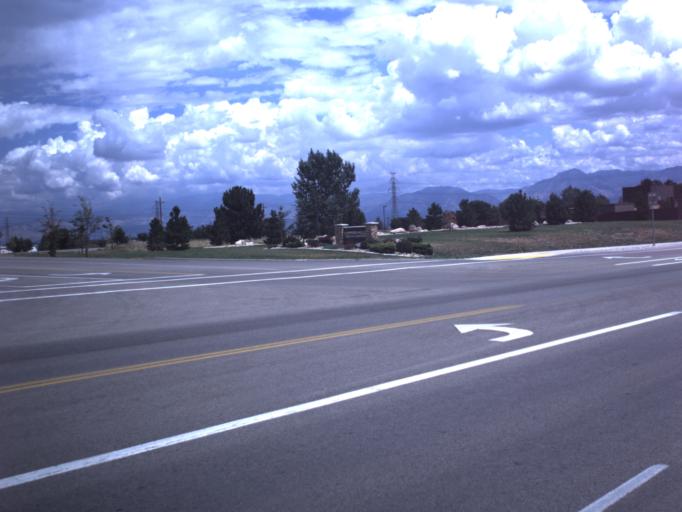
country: US
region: Utah
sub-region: Salt Lake County
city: Oquirrh
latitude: 40.5877
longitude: -112.0354
